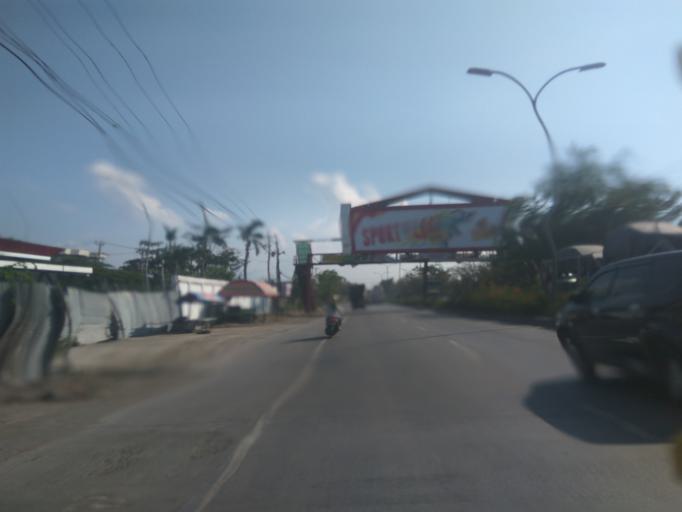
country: ID
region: Central Java
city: Mranggen
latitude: -6.9477
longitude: 110.4909
